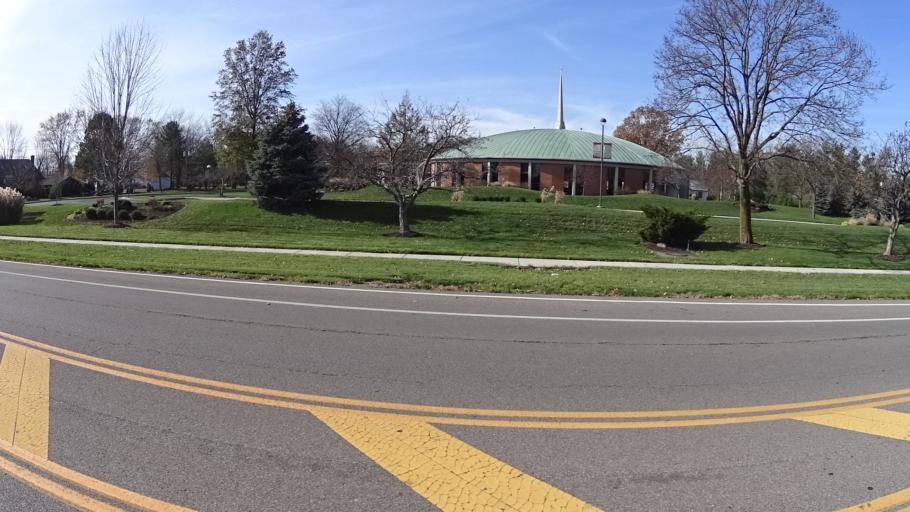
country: US
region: Ohio
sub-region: Lorain County
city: Avon Lake
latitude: 41.4939
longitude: -81.9884
